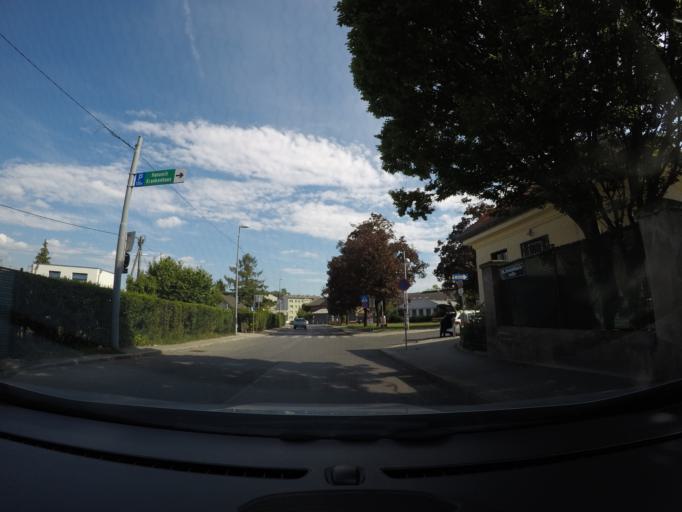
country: AT
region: Vienna
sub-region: Wien Stadt
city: Vienna
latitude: 48.1992
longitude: 16.2938
